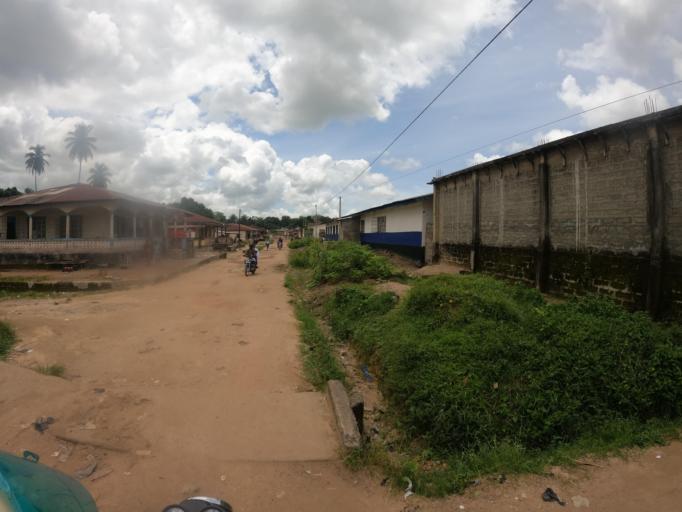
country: SL
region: Northern Province
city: Makeni
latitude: 8.8909
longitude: -12.0520
